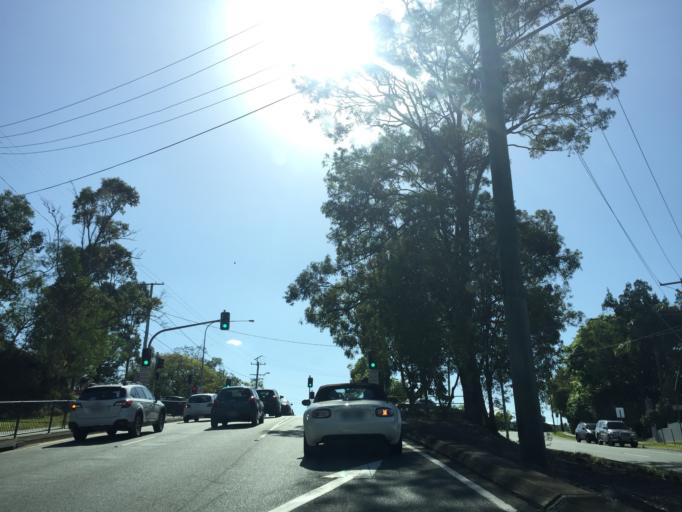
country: AU
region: Queensland
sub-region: Brisbane
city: Milton
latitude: -27.4483
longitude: 152.9758
